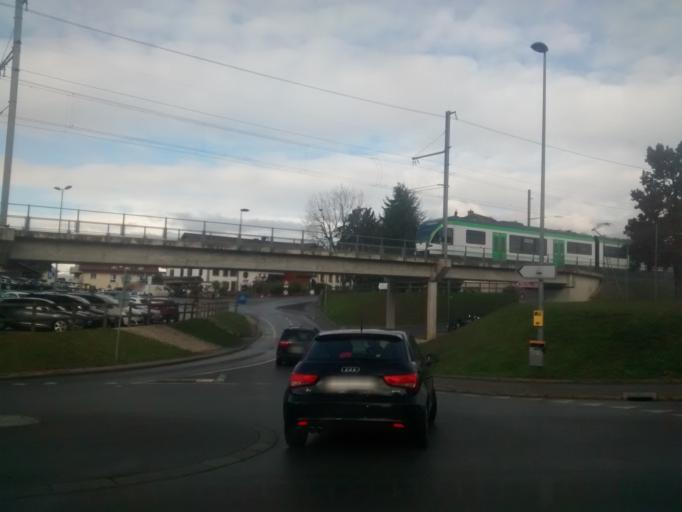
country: CH
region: Vaud
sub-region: Lausanne District
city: Cheseaux
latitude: 46.5832
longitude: 6.6061
